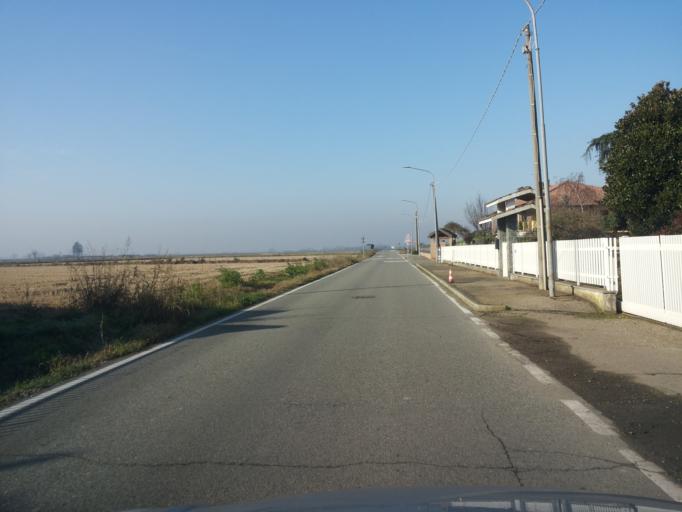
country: IT
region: Piedmont
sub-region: Provincia di Vercelli
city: Stroppiana
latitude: 45.2306
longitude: 8.4480
